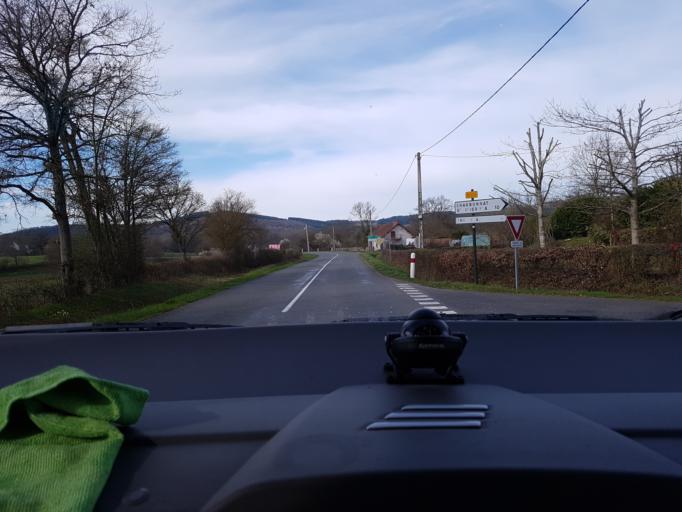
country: FR
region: Bourgogne
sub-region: Departement de Saone-et-Loire
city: Toulon-sur-Arroux
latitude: 46.7532
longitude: 4.1327
